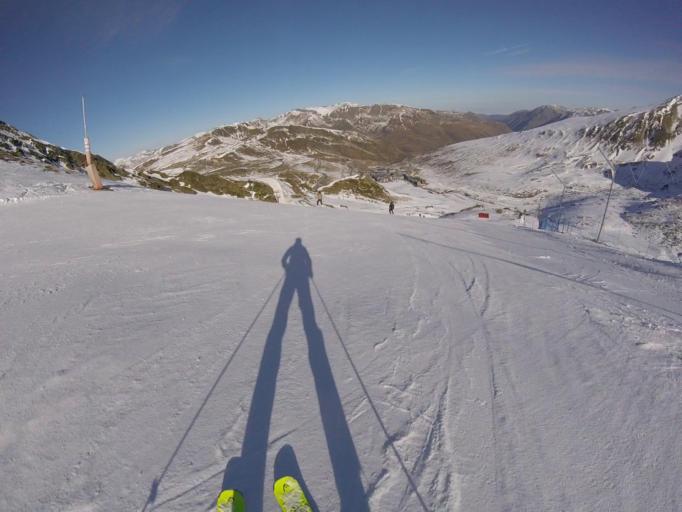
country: AD
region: Encamp
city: Pas de la Casa
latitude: 42.5268
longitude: 1.7254
